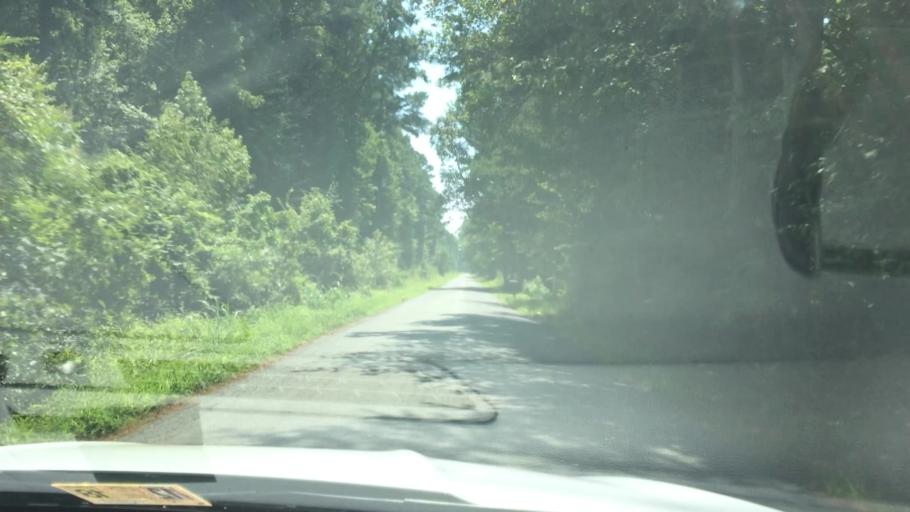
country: US
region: Virginia
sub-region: Charles City County
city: Charles City
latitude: 37.2996
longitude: -76.9658
